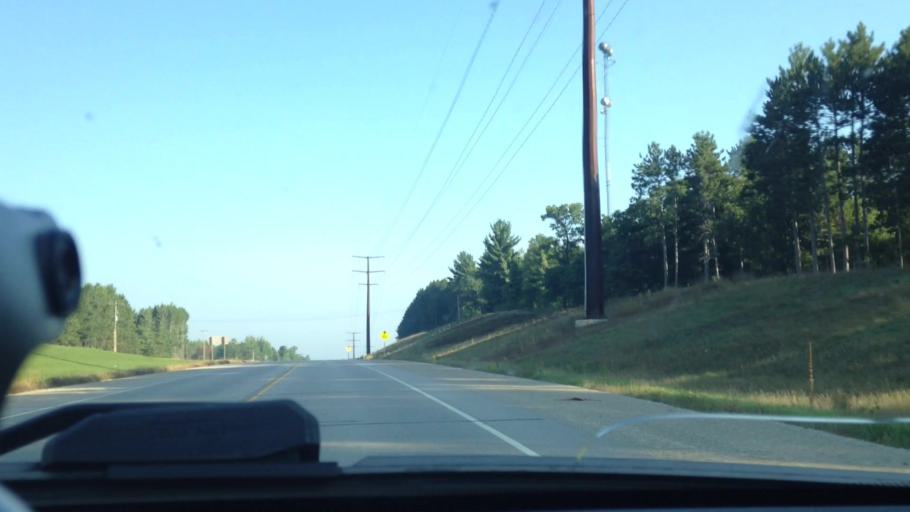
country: US
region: Wisconsin
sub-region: Marinette County
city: Peshtigo
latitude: 45.2118
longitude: -87.9951
